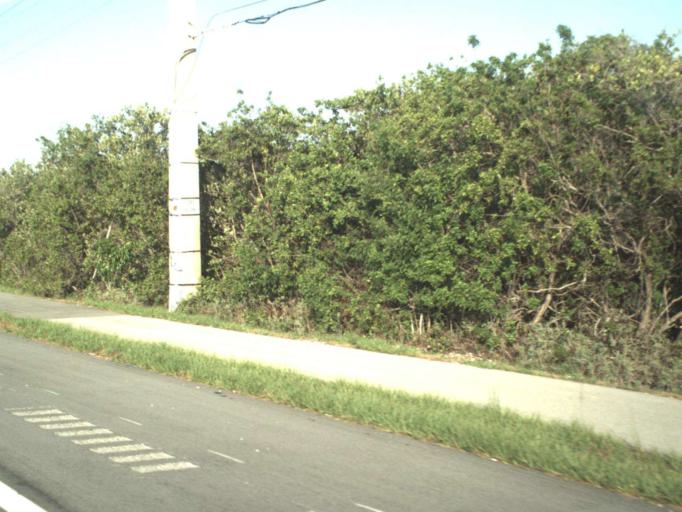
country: US
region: Florida
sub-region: Monroe County
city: Islamorada
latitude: 24.8343
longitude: -80.8028
